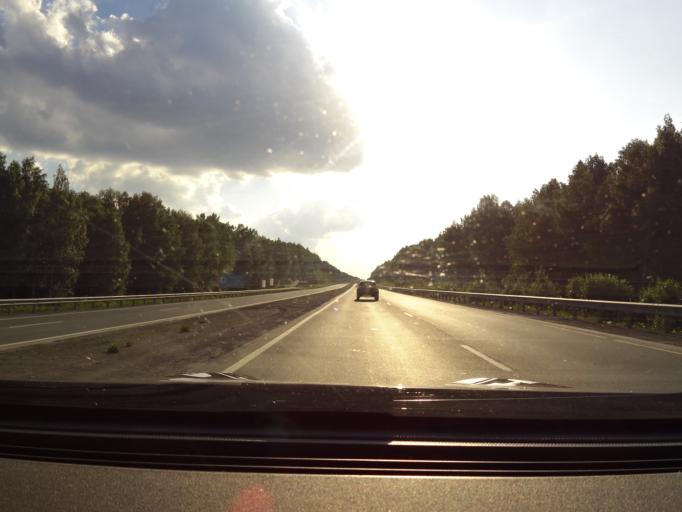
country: RU
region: Sverdlovsk
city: Talitsa
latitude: 56.8380
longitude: 60.1368
